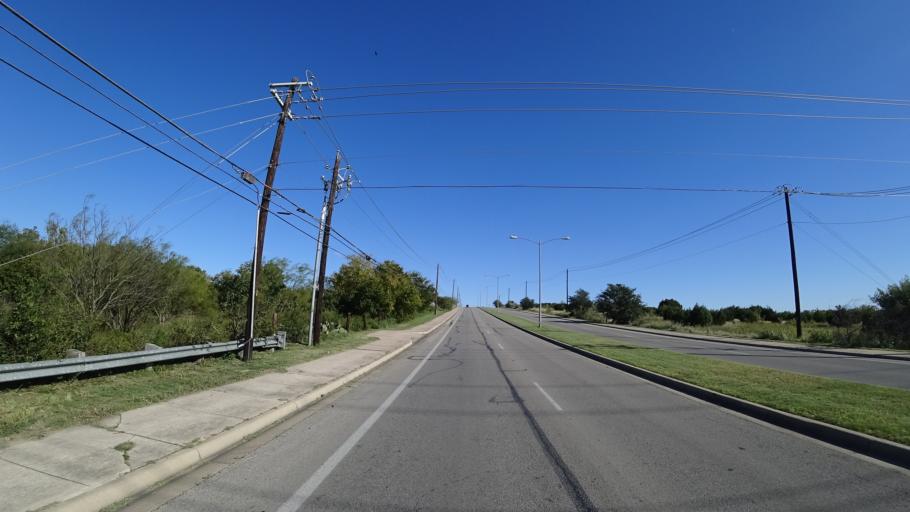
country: US
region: Texas
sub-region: Travis County
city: Hornsby Bend
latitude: 30.2961
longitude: -97.6378
